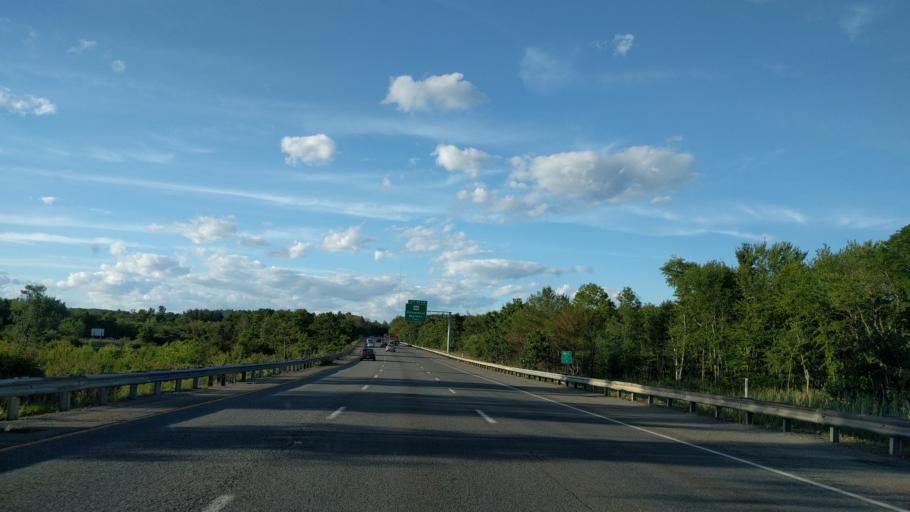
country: US
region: Massachusetts
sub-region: Worcester County
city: Shrewsbury
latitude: 42.3062
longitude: -71.7334
